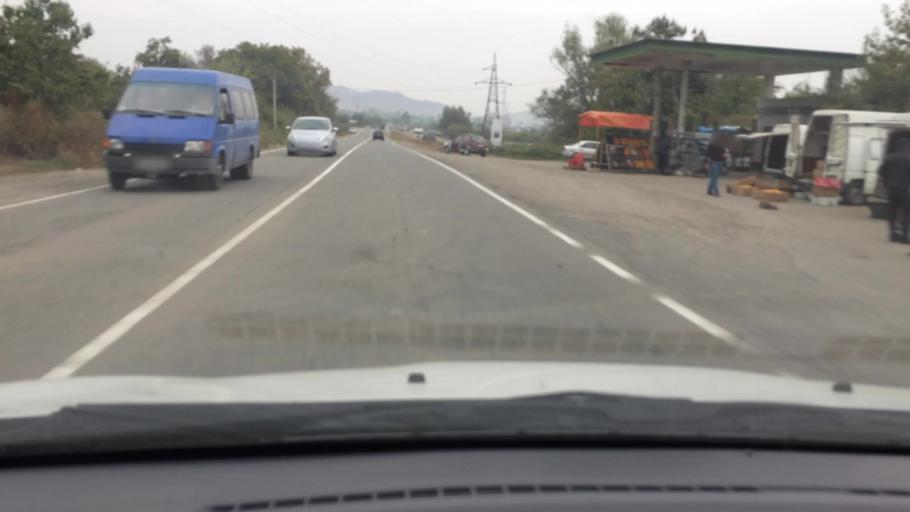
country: GE
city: Naghvarevi
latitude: 41.3066
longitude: 44.7914
